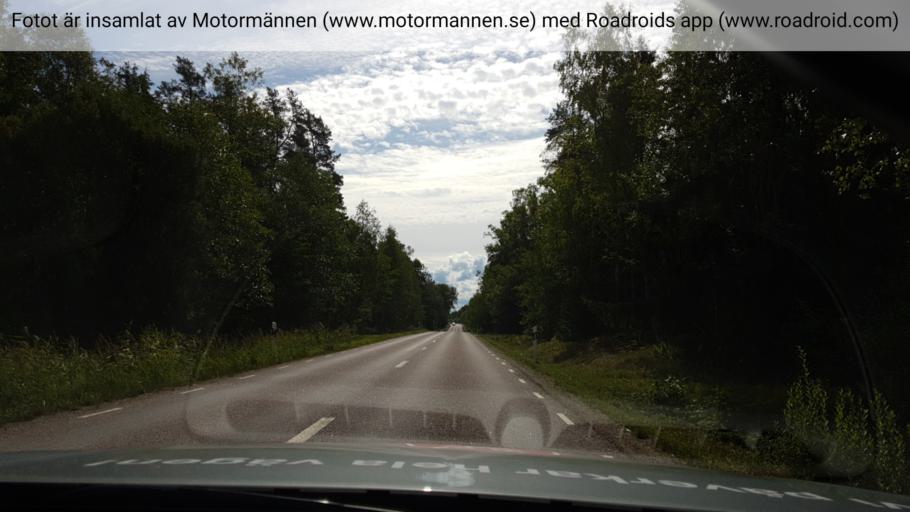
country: SE
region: Uppsala
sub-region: Osthammars Kommun
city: Bjorklinge
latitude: 59.9887
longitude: 17.3246
